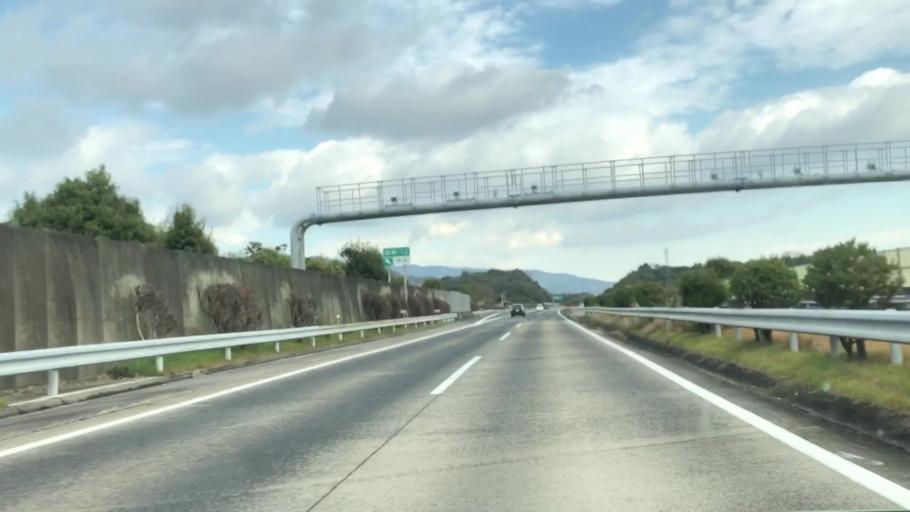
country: JP
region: Saga Prefecture
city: Kanzakimachi-kanzaki
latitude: 33.3470
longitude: 130.3677
